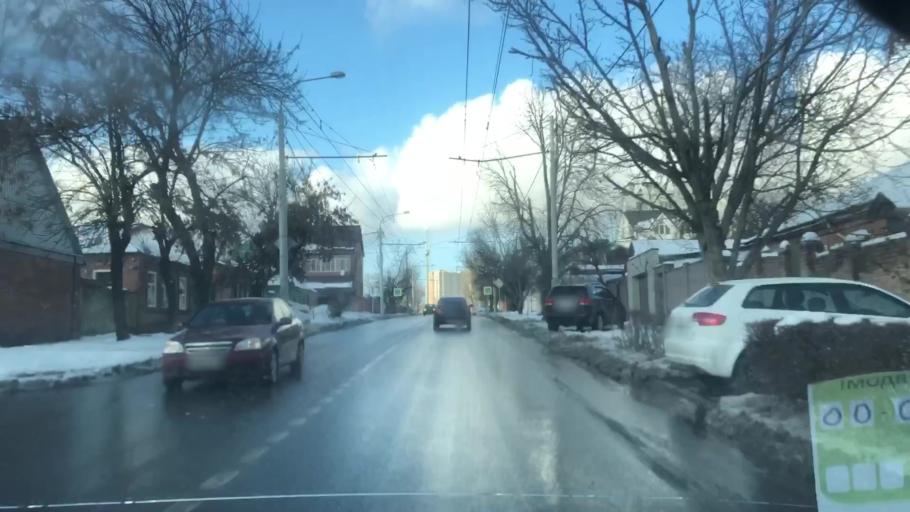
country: RU
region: Rostov
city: Rostov-na-Donu
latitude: 47.2057
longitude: 39.6770
